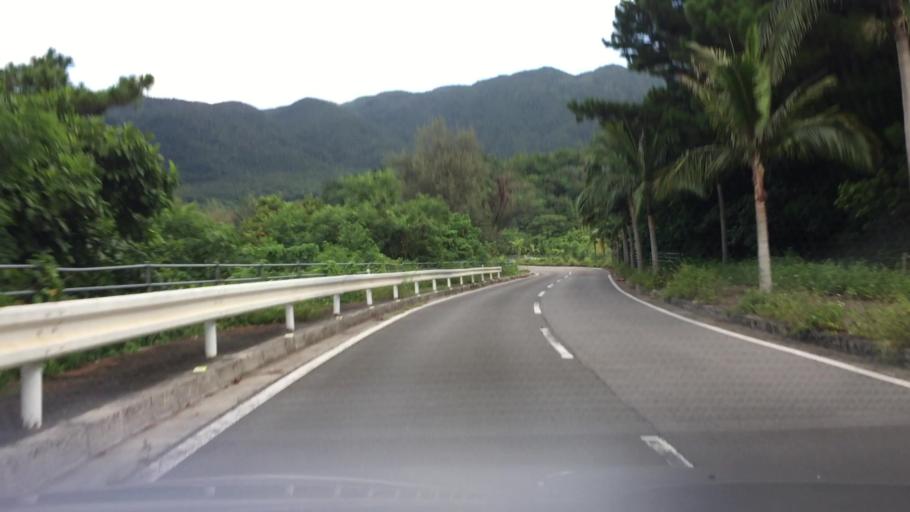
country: JP
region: Okinawa
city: Ishigaki
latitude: 24.4480
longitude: 124.1332
